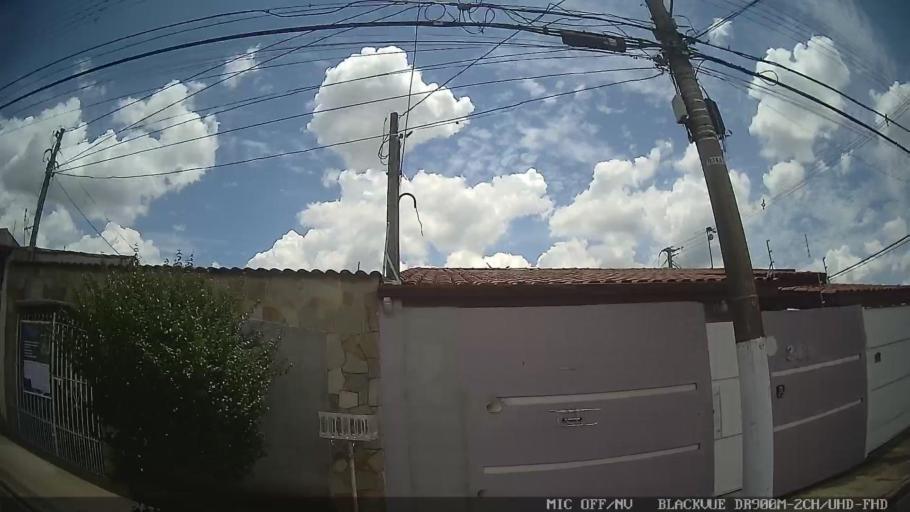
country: BR
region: Sao Paulo
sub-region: Atibaia
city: Atibaia
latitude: -23.1075
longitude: -46.5446
